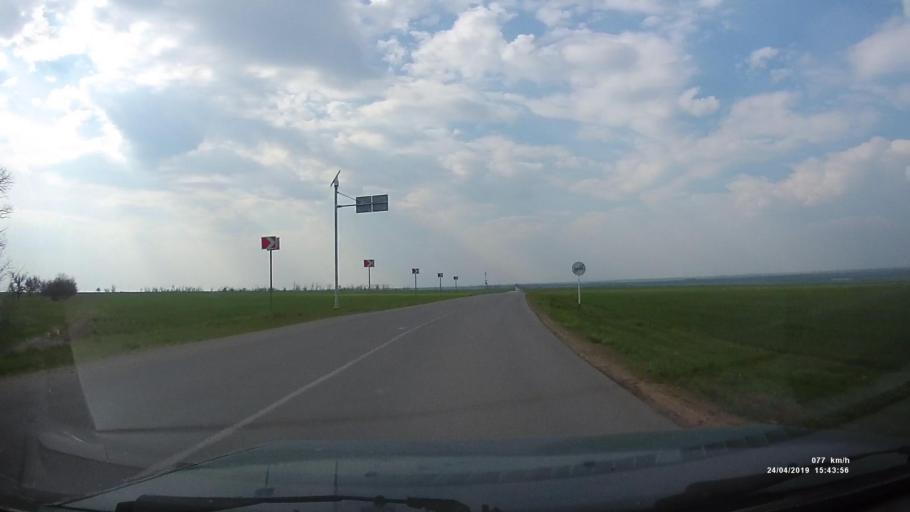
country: RU
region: Kalmykiya
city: Yashalta
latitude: 46.5855
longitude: 42.7640
